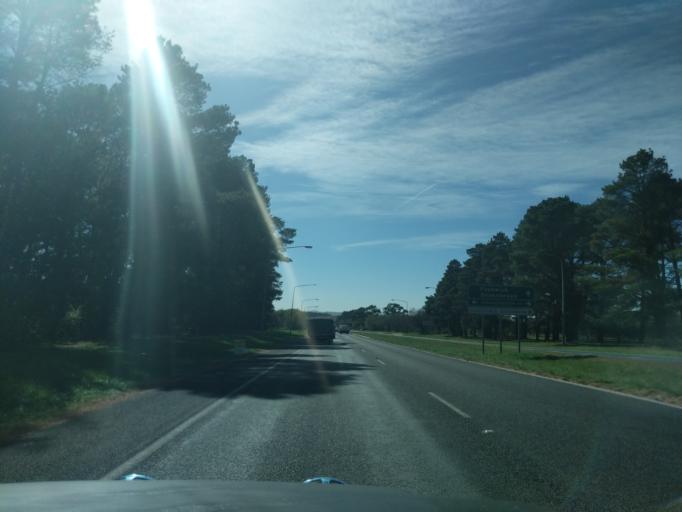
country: AU
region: Australian Capital Territory
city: Forrest
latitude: -35.3442
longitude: 149.1505
